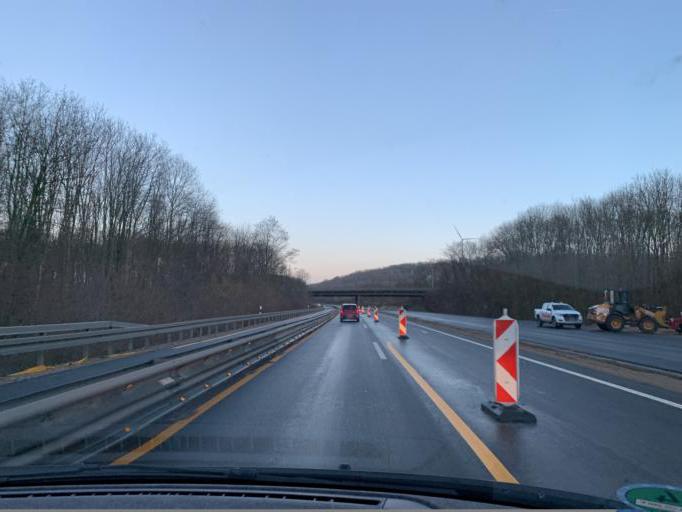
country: DE
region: North Rhine-Westphalia
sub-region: Regierungsbezirk Dusseldorf
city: Grevenbroich
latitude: 51.0767
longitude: 6.5894
